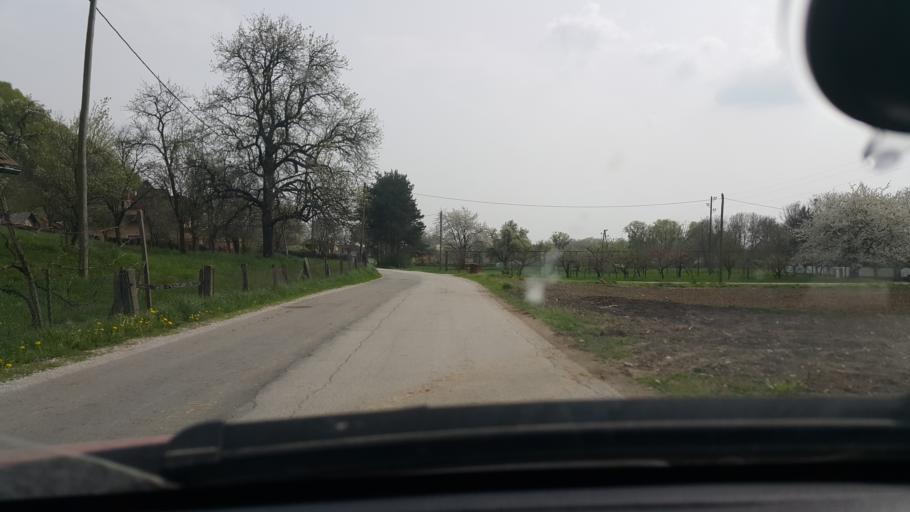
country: SI
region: Duplek
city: Zgornji Duplek
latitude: 46.5187
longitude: 15.7169
